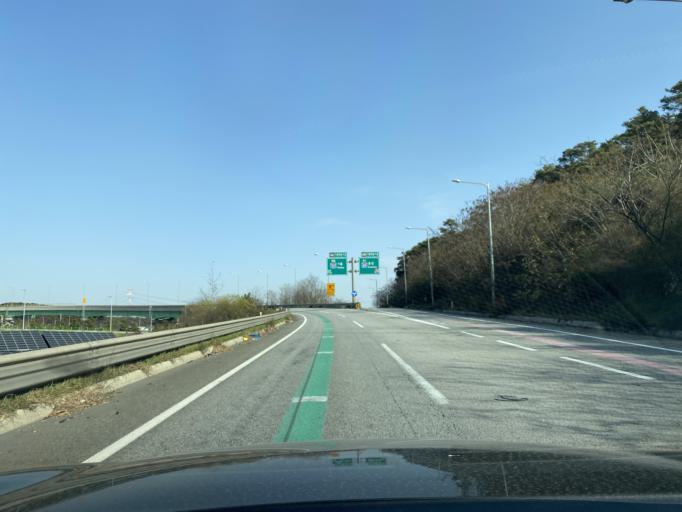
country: KR
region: Gyeonggi-do
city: Hwaseong-si
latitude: 37.0516
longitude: 126.8886
